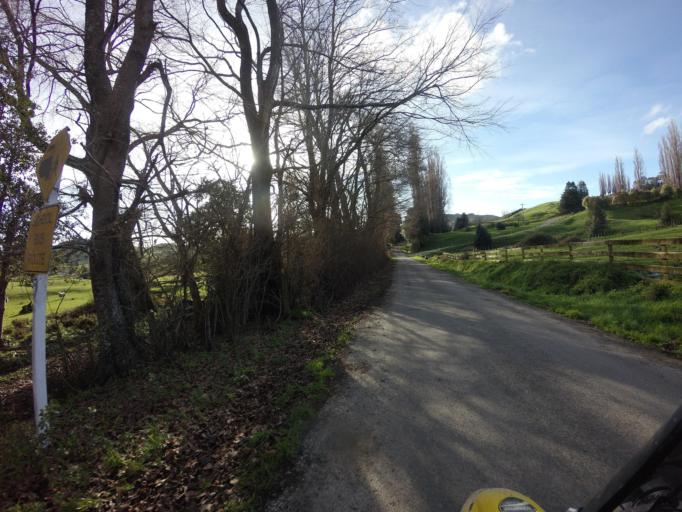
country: NZ
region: Hawke's Bay
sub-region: Wairoa District
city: Wairoa
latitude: -38.7734
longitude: 177.5660
